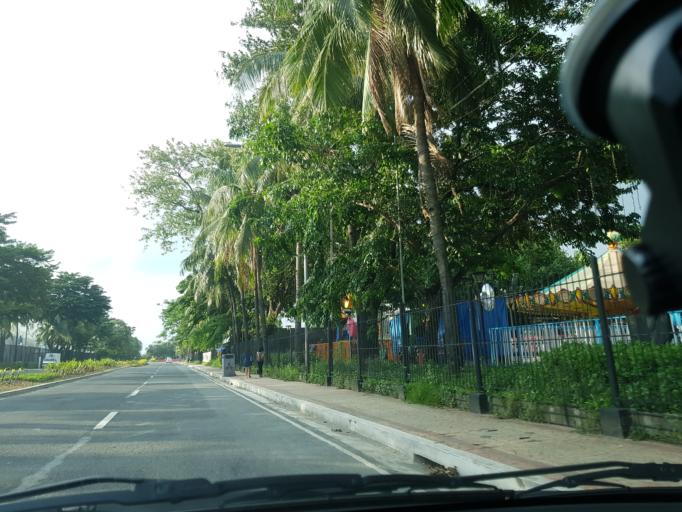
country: PH
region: Metro Manila
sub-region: City of Manila
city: Port Area
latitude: 14.5546
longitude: 120.9852
